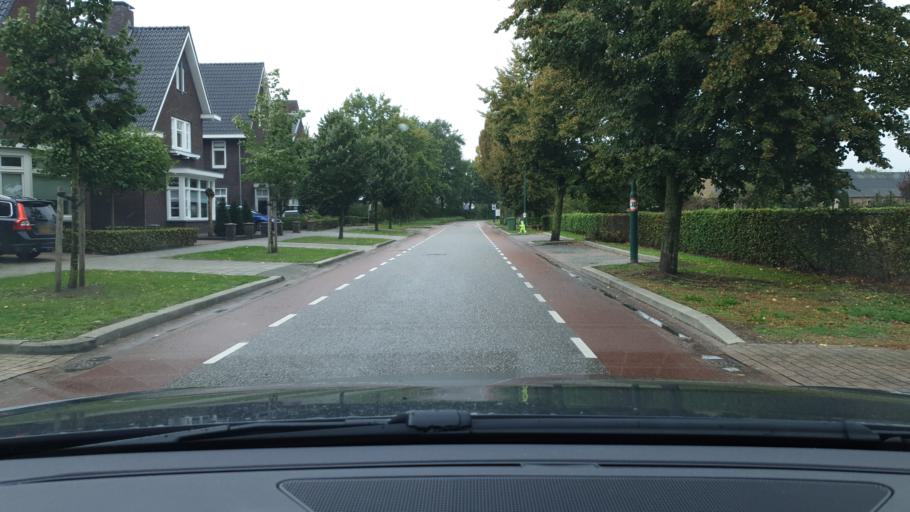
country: NL
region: North Brabant
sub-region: Gemeente Sint-Oedenrode
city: Sint-Oedenrode
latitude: 51.5538
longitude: 5.4876
